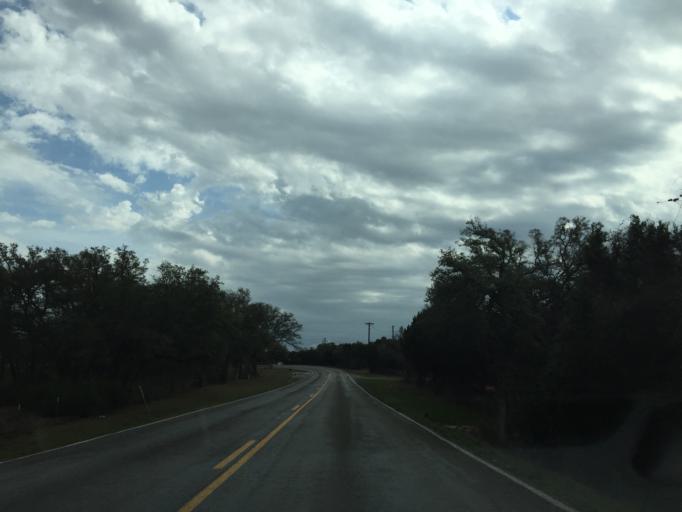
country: US
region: Texas
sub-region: Burnet County
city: Bertram
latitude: 30.6512
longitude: -97.9849
